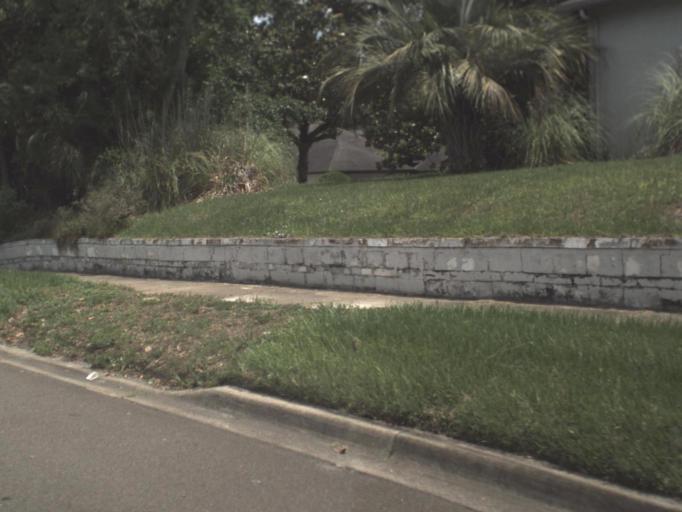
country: US
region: Florida
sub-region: Duval County
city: Jacksonville
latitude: 30.2956
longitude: -81.6476
